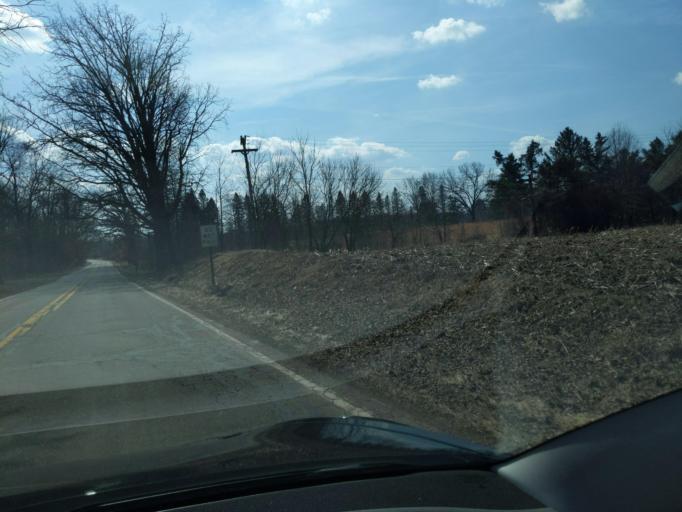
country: US
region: Michigan
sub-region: Livingston County
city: Pinckney
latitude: 42.4404
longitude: -84.0600
